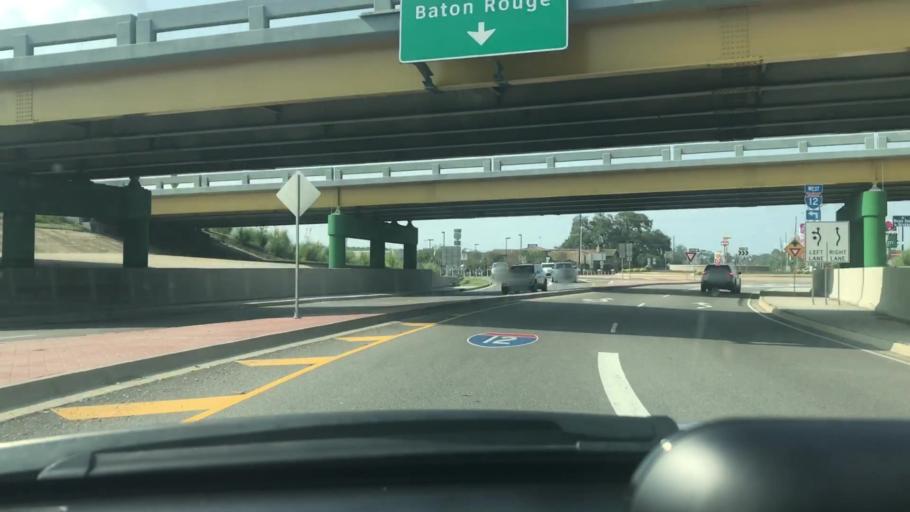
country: US
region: Louisiana
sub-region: Tangipahoa Parish
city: Hammond
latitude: 30.4787
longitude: -90.4570
